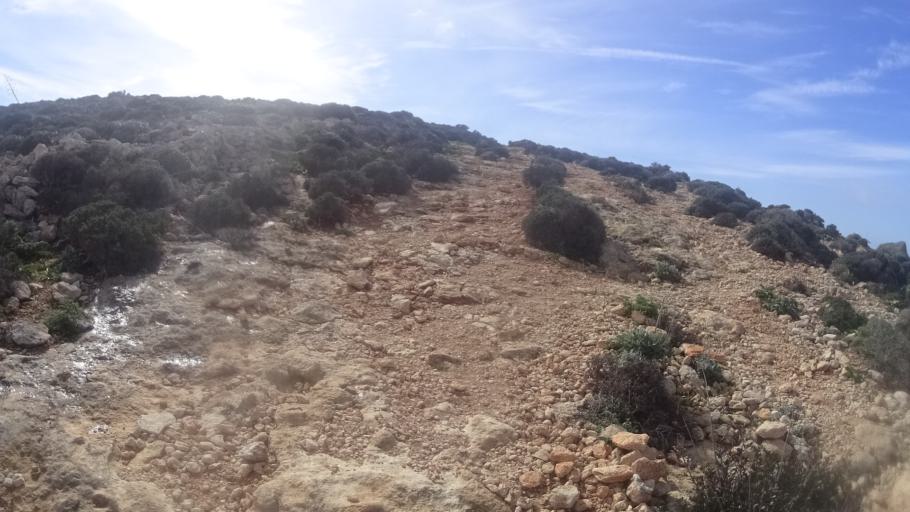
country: MT
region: Il-Qala
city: Qala
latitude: 36.0091
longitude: 14.3300
